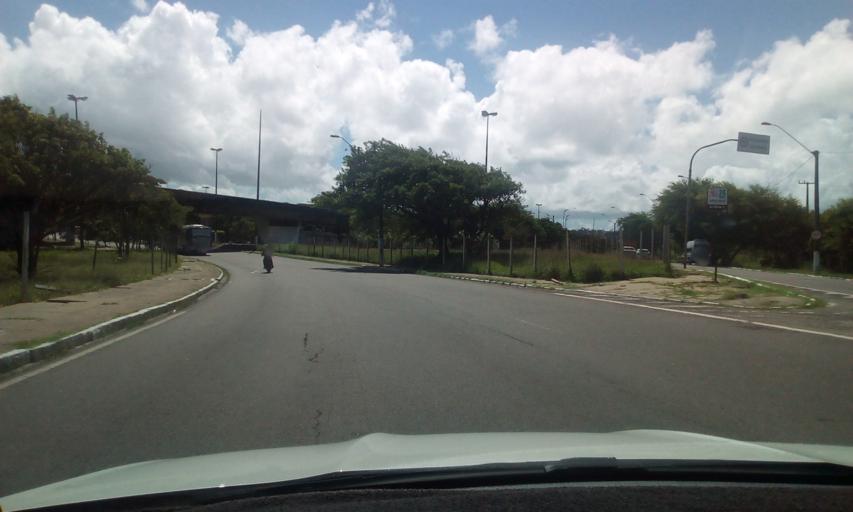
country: BR
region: Pernambuco
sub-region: Olinda
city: Olinda
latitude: -8.0302
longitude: -34.8647
